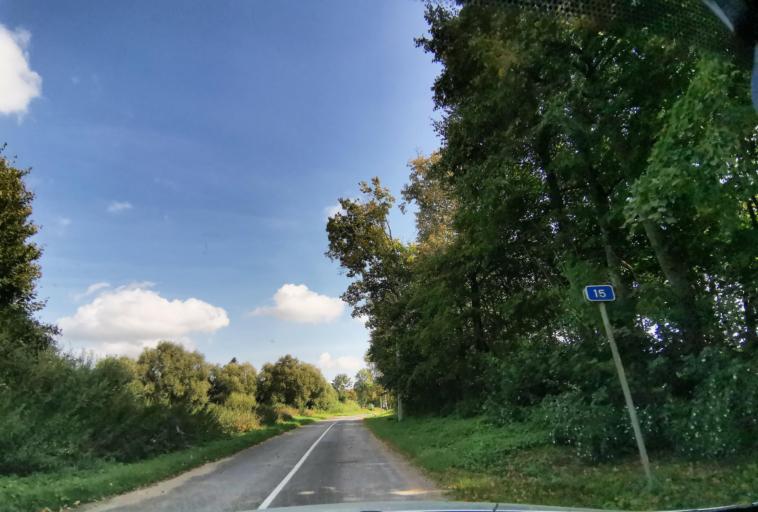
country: RU
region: Kaliningrad
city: Gusev
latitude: 54.6506
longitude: 22.0529
